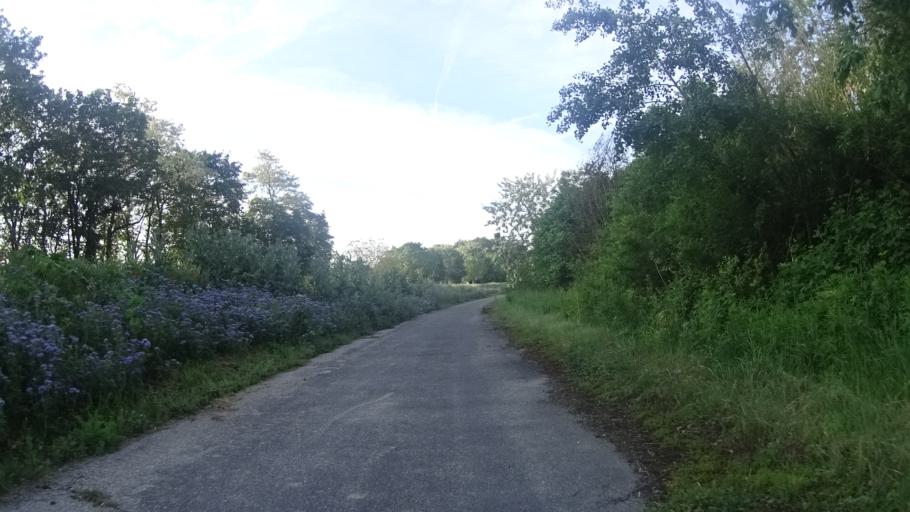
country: DE
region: Baden-Wuerttemberg
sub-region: Freiburg Region
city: Hartheim
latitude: 47.9782
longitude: 7.6443
